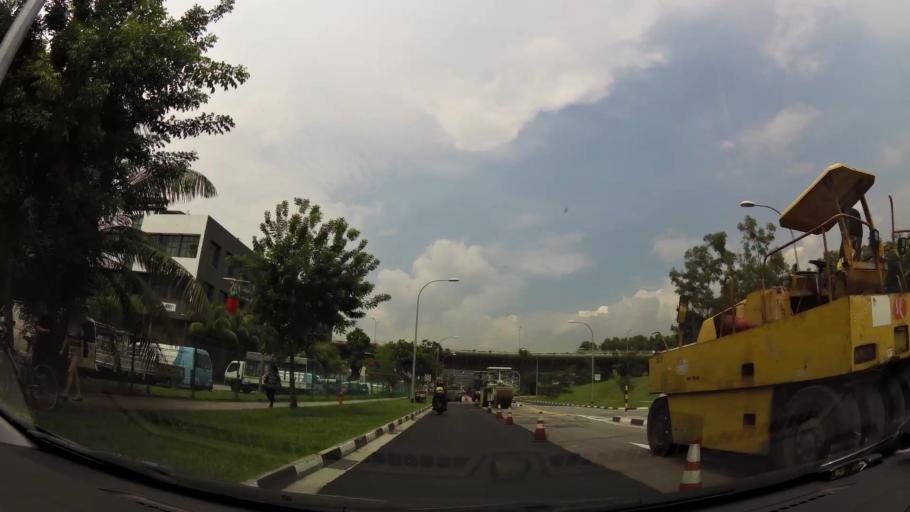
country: SG
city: Singapore
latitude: 1.3379
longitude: 103.9129
